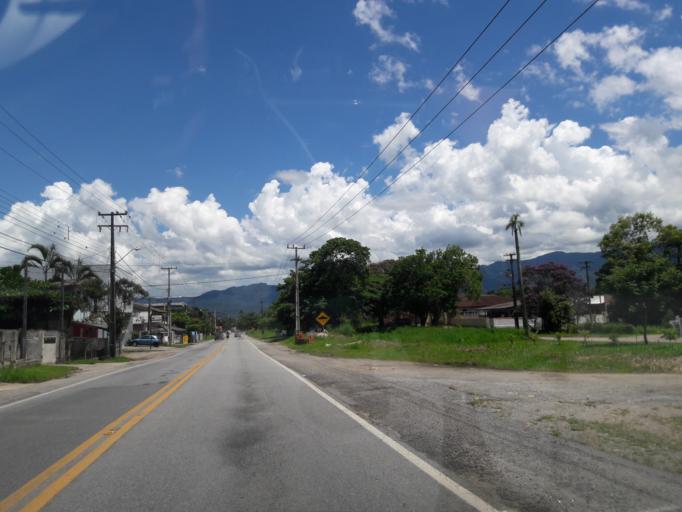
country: BR
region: Parana
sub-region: Antonina
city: Antonina
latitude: -25.4682
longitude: -48.8277
